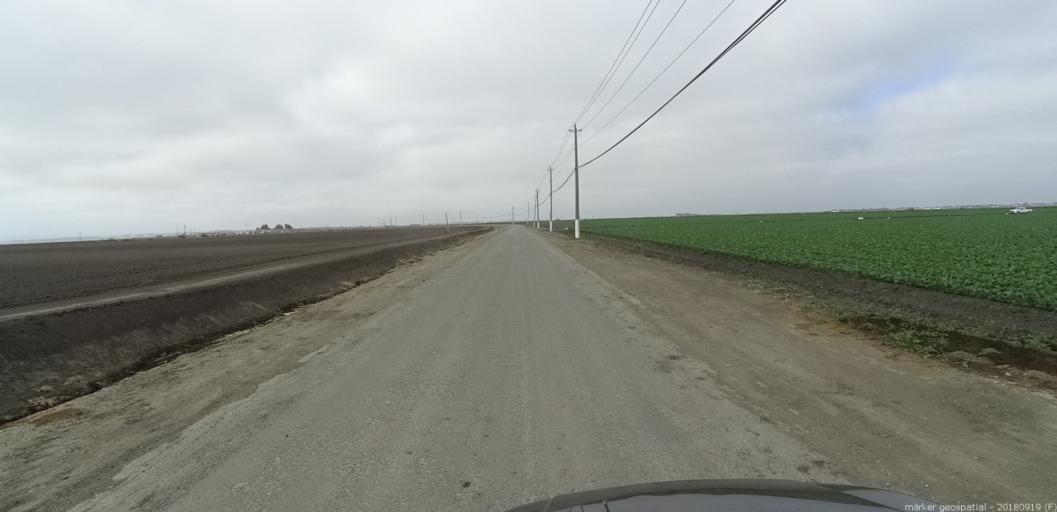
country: US
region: California
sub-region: Monterey County
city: Castroville
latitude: 36.7641
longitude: -121.7608
